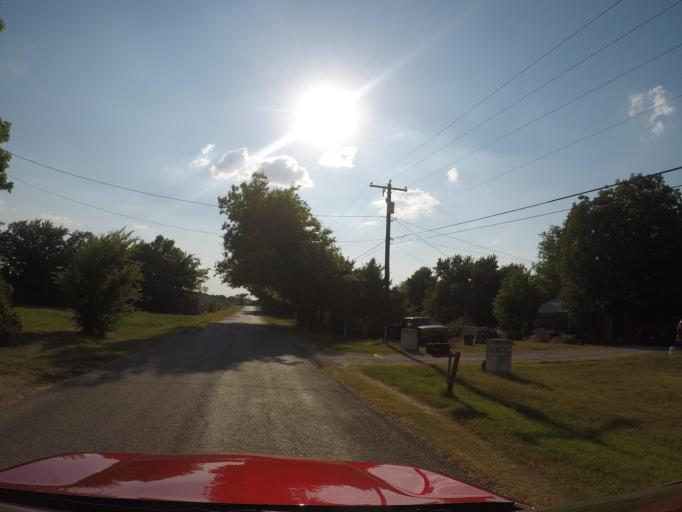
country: US
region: Texas
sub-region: Grayson County
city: Pottsboro
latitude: 33.7976
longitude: -96.6100
